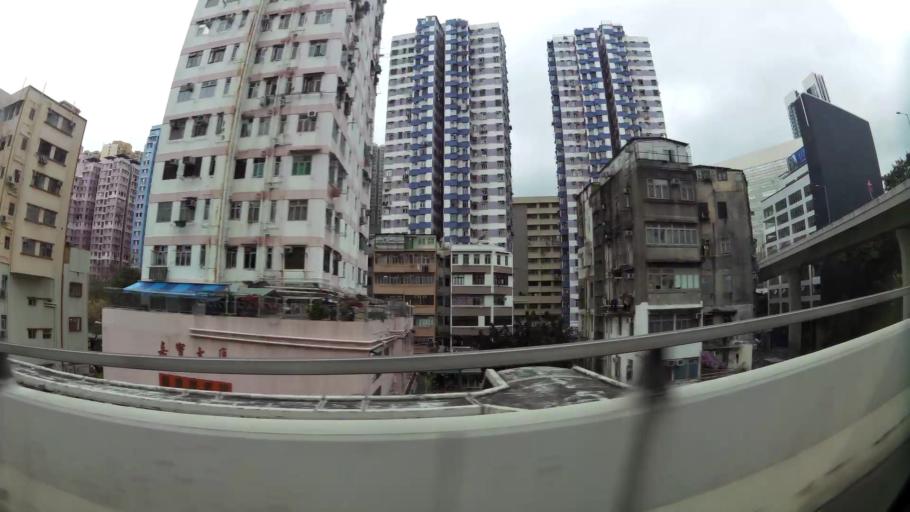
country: HK
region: Tsuen Wan
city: Tsuen Wan
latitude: 22.3685
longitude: 114.1340
